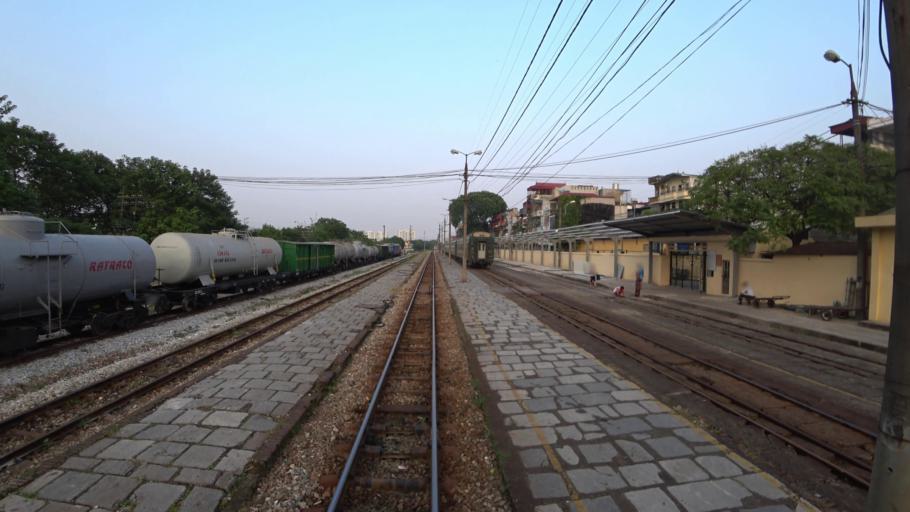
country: VN
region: Ha Noi
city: Hoan Kiem
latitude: 21.0603
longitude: 105.8918
